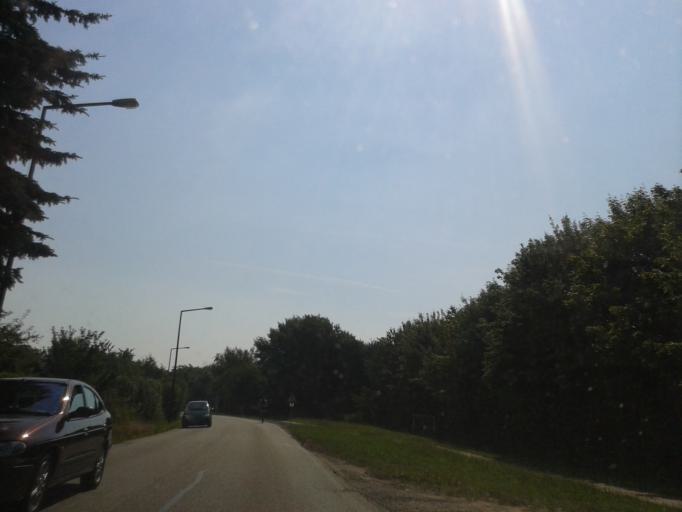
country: DE
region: Saxony
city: Bannewitz
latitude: 51.0187
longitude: 13.7129
